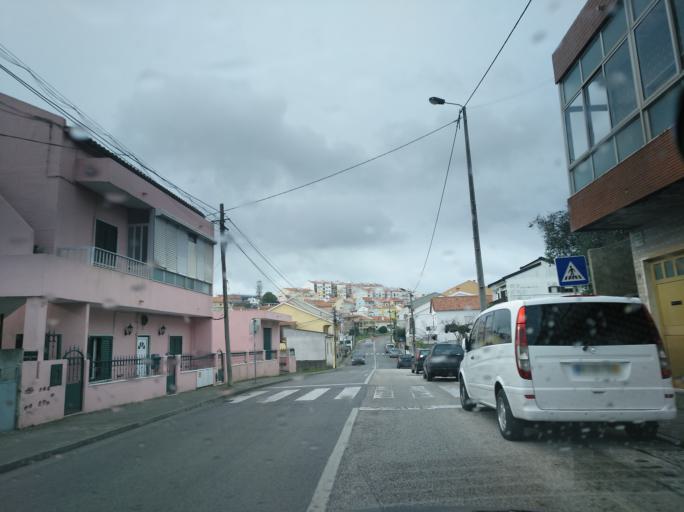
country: PT
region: Lisbon
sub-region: Odivelas
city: Famoes
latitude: 38.7957
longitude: -9.2245
